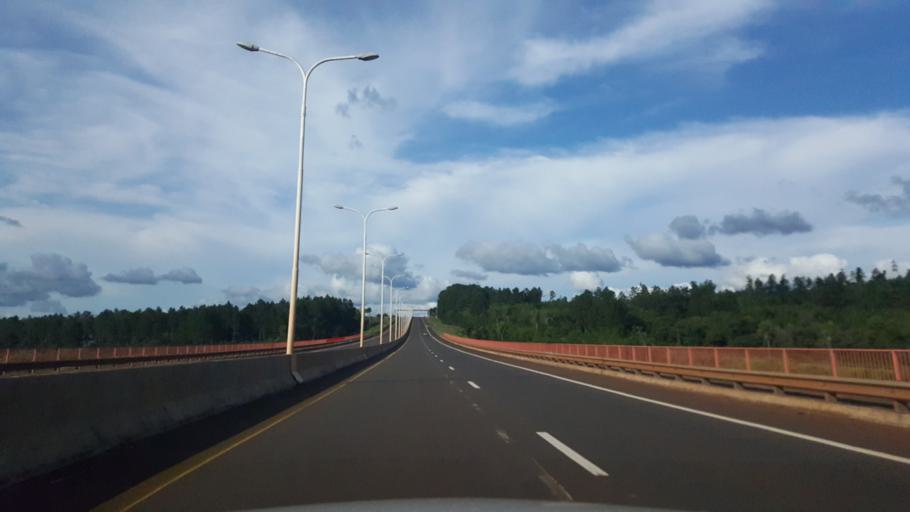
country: AR
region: Misiones
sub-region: Departamento de Candelaria
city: Loreto
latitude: -27.3062
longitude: -55.5402
